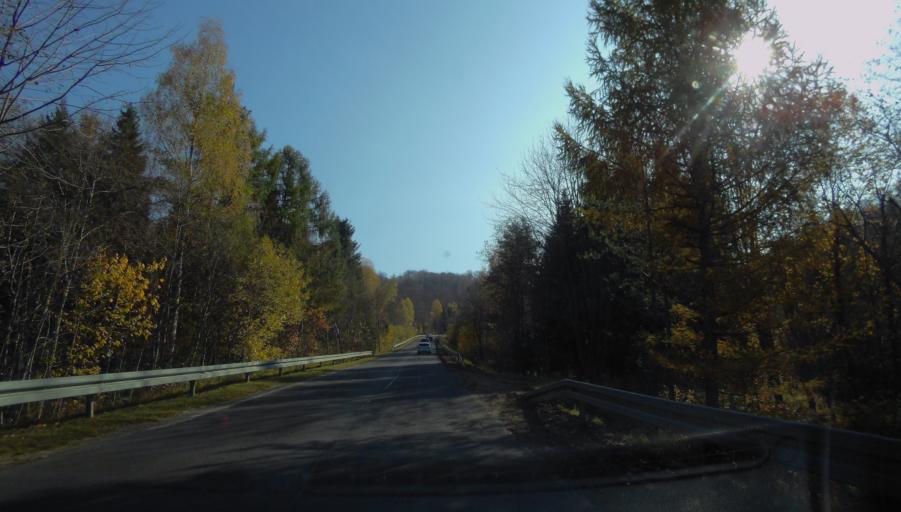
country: PL
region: Subcarpathian Voivodeship
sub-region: Powiat leski
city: Cisna
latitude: 49.2159
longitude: 22.2347
